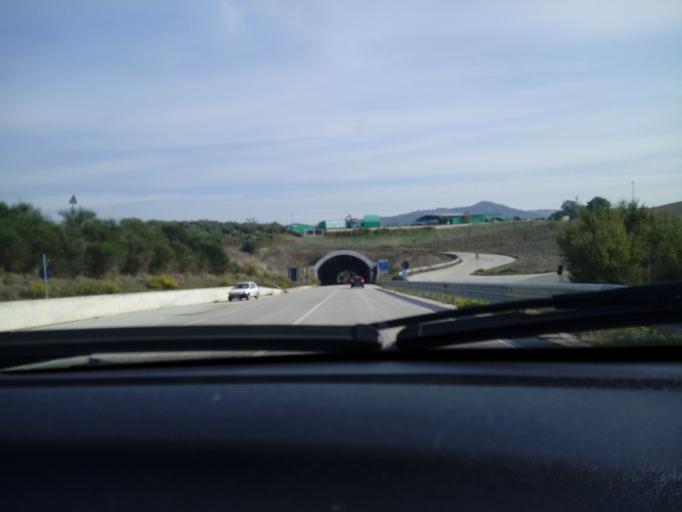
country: IT
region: Molise
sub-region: Provincia di Campobasso
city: Gambatesa
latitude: 41.5291
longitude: 14.8765
